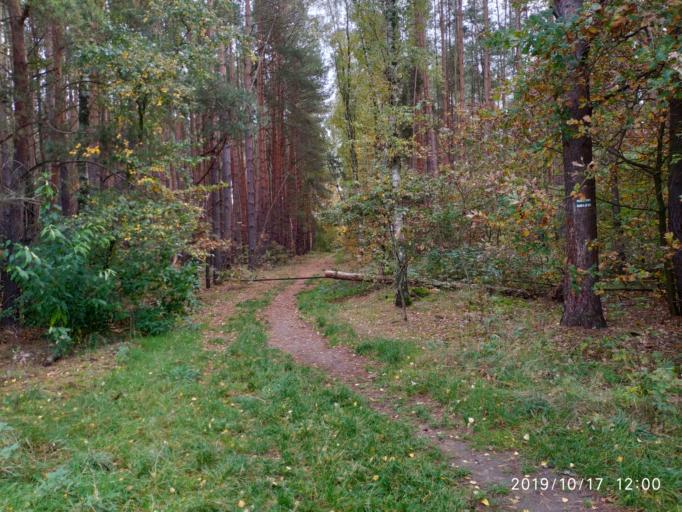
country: PL
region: Lubusz
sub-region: Zielona Gora
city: Zielona Gora
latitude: 51.9420
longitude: 15.5649
